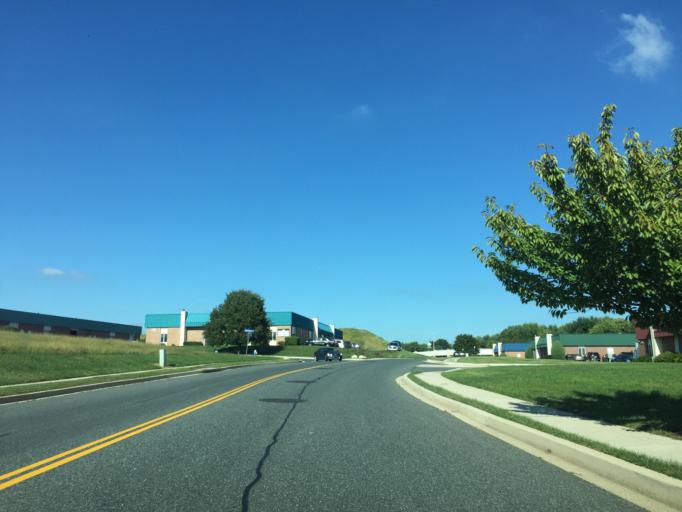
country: US
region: Maryland
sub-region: Harford County
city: Bel Air North
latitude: 39.5756
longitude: -76.3698
